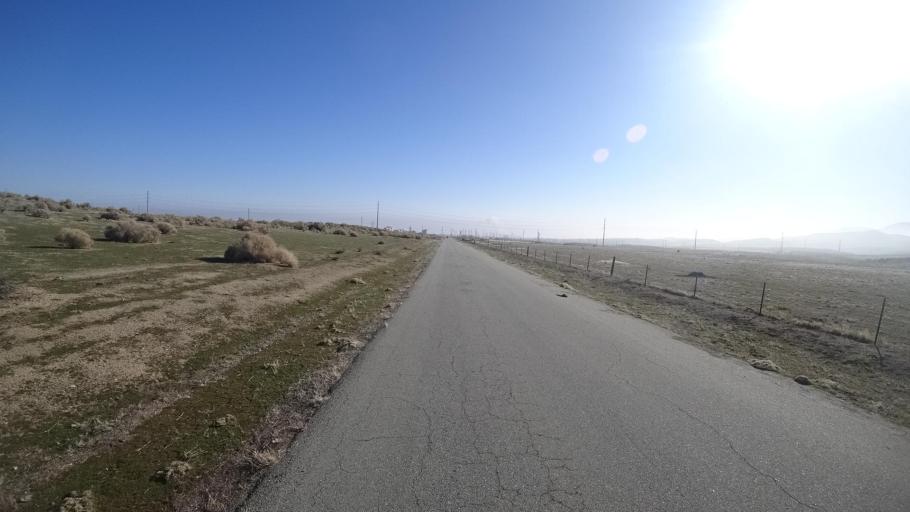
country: US
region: California
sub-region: Kern County
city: Taft Heights
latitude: 35.2271
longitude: -119.6379
